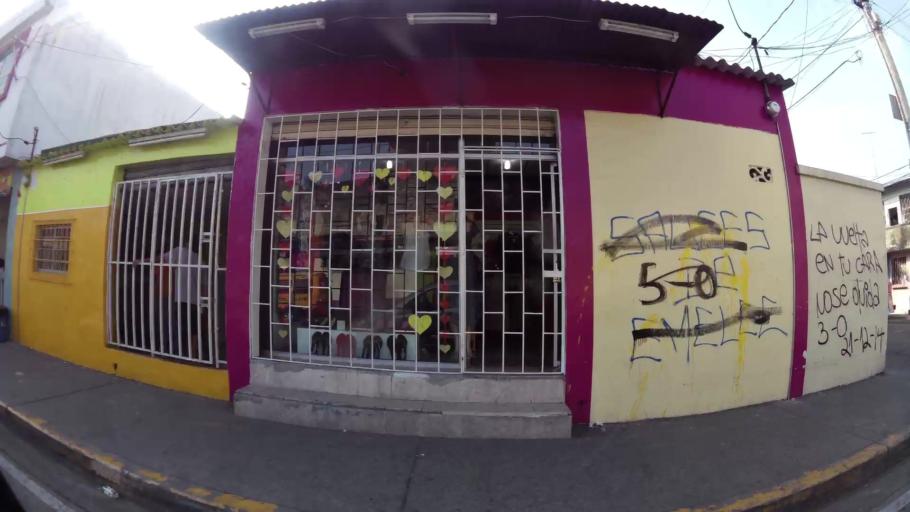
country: EC
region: Guayas
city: Eloy Alfaro
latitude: -2.1252
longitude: -79.8949
